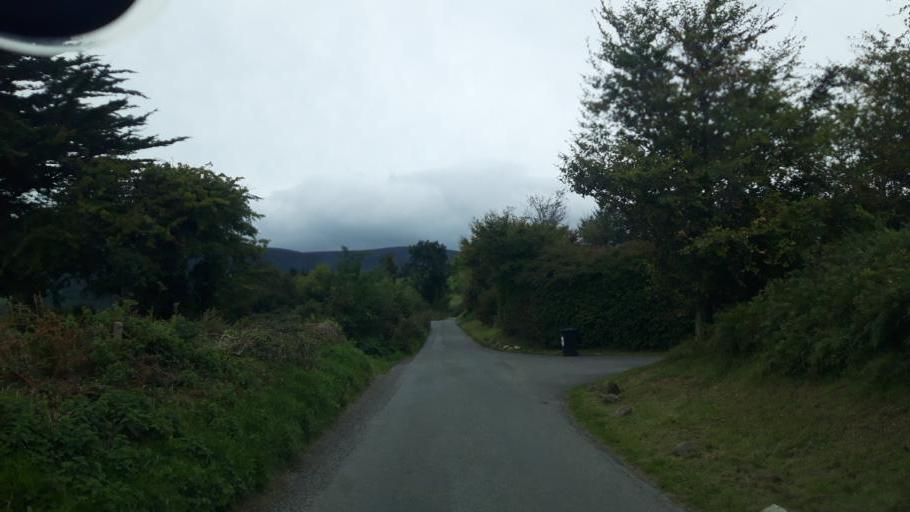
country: IE
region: Leinster
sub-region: Wicklow
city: Enniskerry
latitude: 53.1846
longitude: -6.2046
